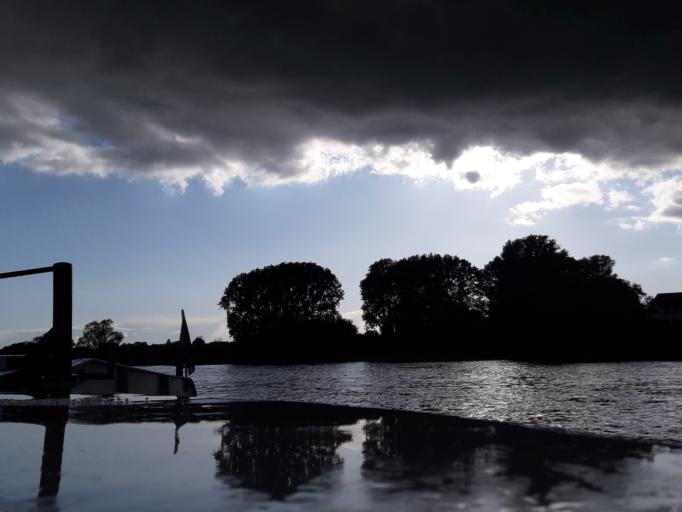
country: DE
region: North Rhine-Westphalia
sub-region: Regierungsbezirk Dusseldorf
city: Meerbusch
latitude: 51.2980
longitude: 6.7267
